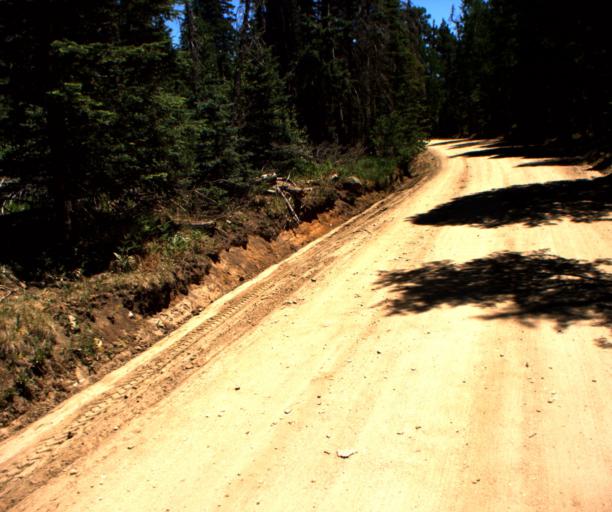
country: US
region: Arizona
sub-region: Graham County
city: Swift Trail Junction
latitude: 32.6988
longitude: -109.9100
